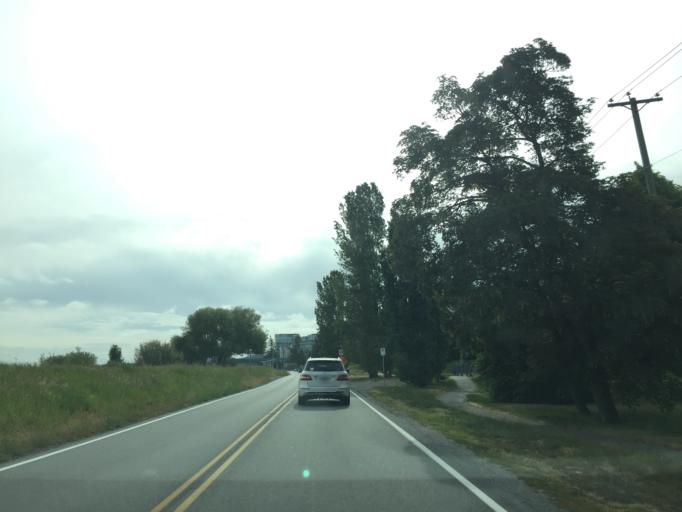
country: CA
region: British Columbia
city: Richmond
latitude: 49.1735
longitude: -123.1641
